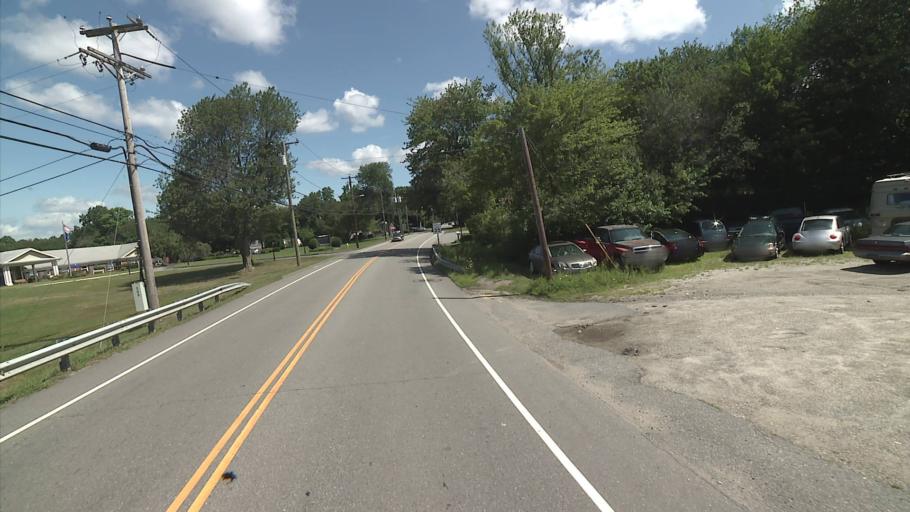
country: US
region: Connecticut
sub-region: Middlesex County
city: Westbrook Center
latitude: 41.2837
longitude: -72.4214
